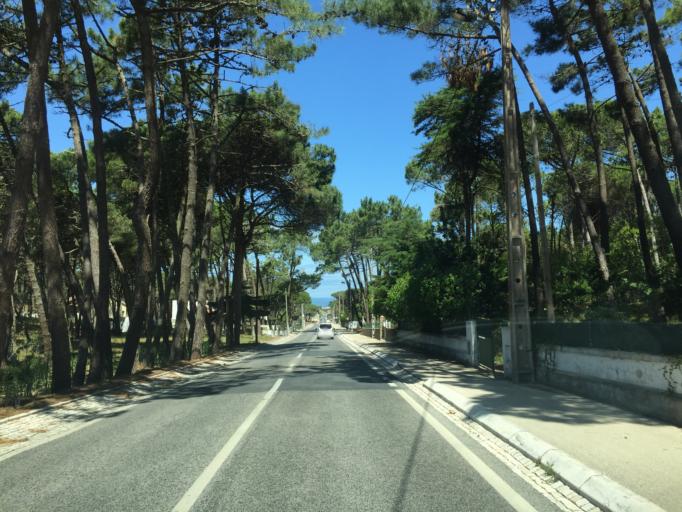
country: PT
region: Lisbon
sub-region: Sintra
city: Colares
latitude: 38.8330
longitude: -9.4530
